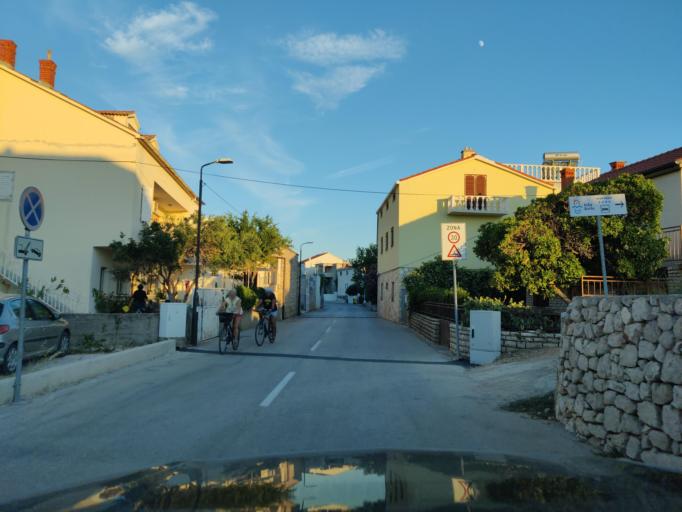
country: HR
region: Sibensko-Kniniska
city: Murter
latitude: 43.8209
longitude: 15.6032
